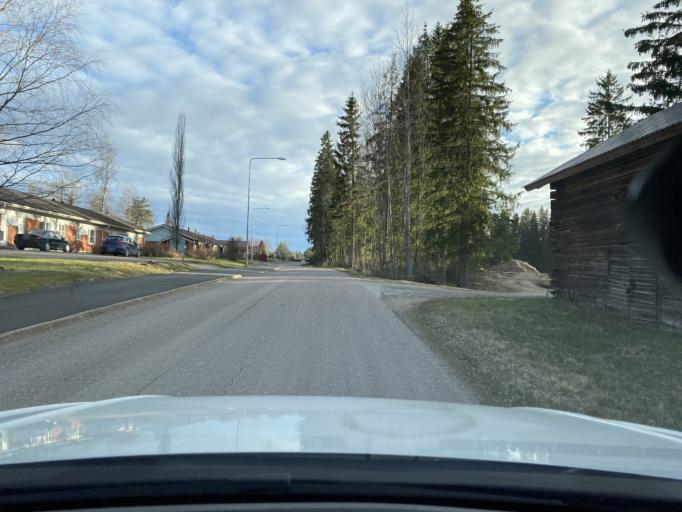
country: FI
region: Pirkanmaa
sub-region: Lounais-Pirkanmaa
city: Punkalaidun
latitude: 61.1164
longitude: 23.1038
